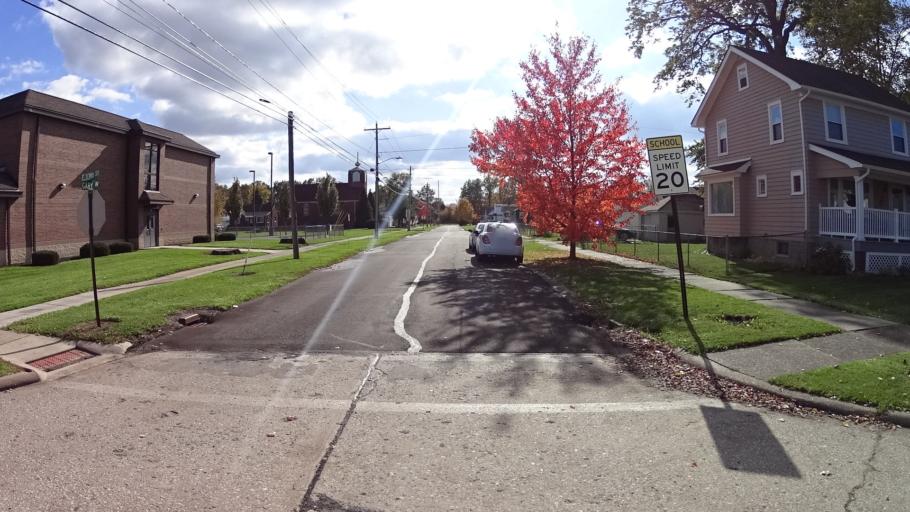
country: US
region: Ohio
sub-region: Lorain County
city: Sheffield
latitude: 41.4406
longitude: -82.1174
